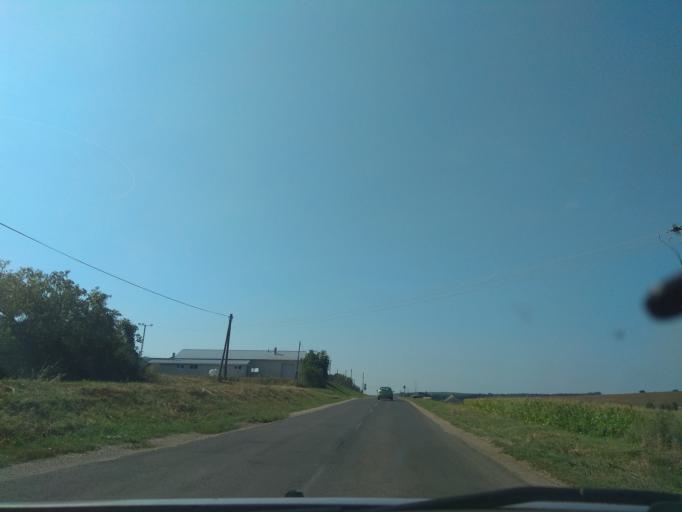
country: HU
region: Borsod-Abauj-Zemplen
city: Harsany
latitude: 47.9519
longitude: 20.7454
